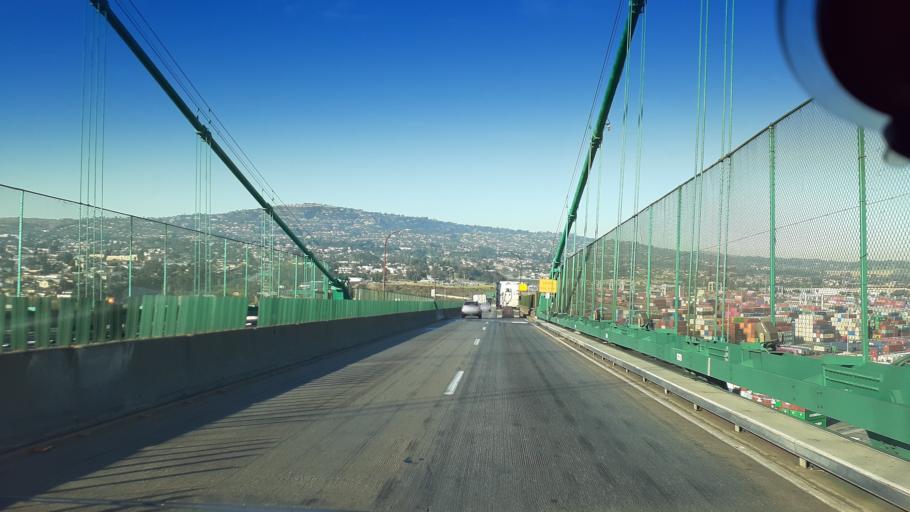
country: US
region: California
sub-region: Los Angeles County
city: San Pedro
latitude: 33.7500
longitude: -118.2747
